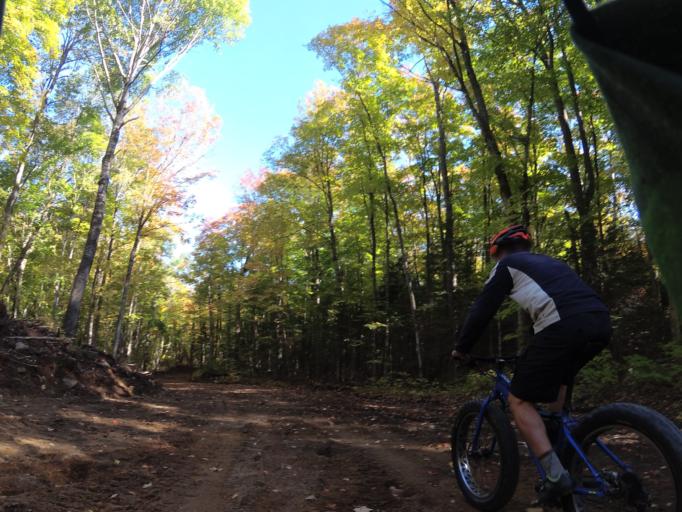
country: CA
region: Ontario
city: Pembroke
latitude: 45.3476
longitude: -77.1670
